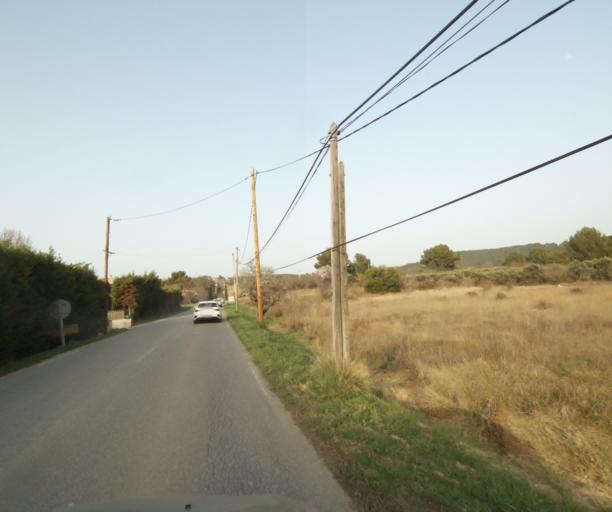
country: FR
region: Provence-Alpes-Cote d'Azur
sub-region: Departement des Bouches-du-Rhone
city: Eguilles
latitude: 43.5591
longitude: 5.3514
